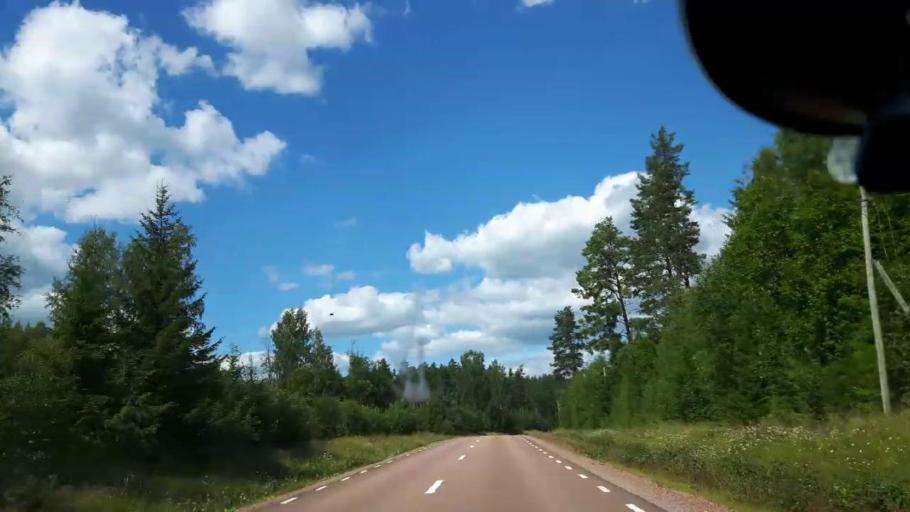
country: SE
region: Jaemtland
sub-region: Ragunda Kommun
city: Hammarstrand
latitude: 63.0325
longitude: 16.5199
